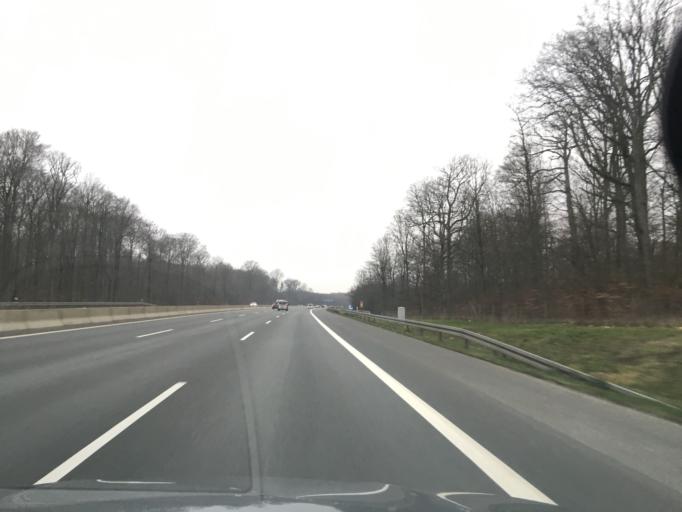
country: DE
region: Bavaria
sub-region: Regierungsbezirk Unterfranken
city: Wuerzburg
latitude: 49.7497
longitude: 9.8896
